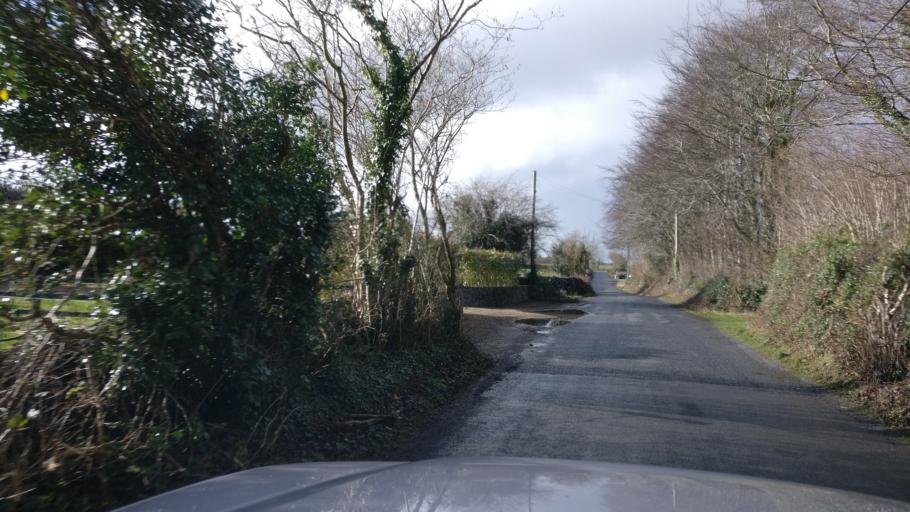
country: IE
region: Connaught
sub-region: County Galway
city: Oranmore
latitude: 53.2366
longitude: -8.8253
